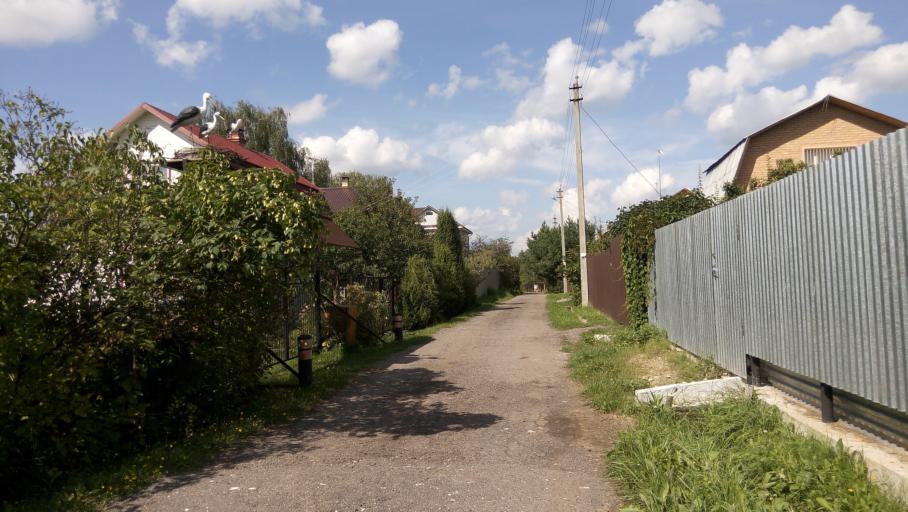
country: RU
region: Moskovskaya
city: Proletarskiy
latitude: 55.0566
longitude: 37.4008
